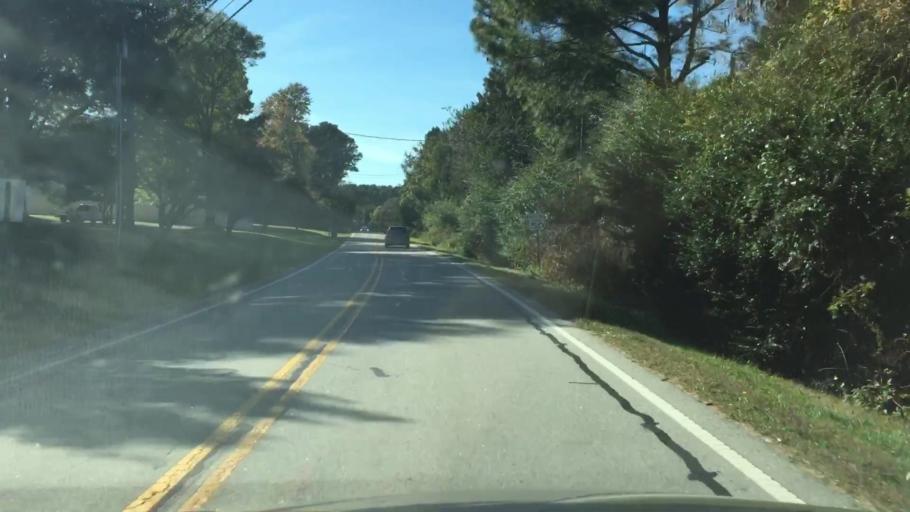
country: US
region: North Carolina
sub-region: Rowan County
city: Salisbury
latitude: 35.6616
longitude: -80.5452
